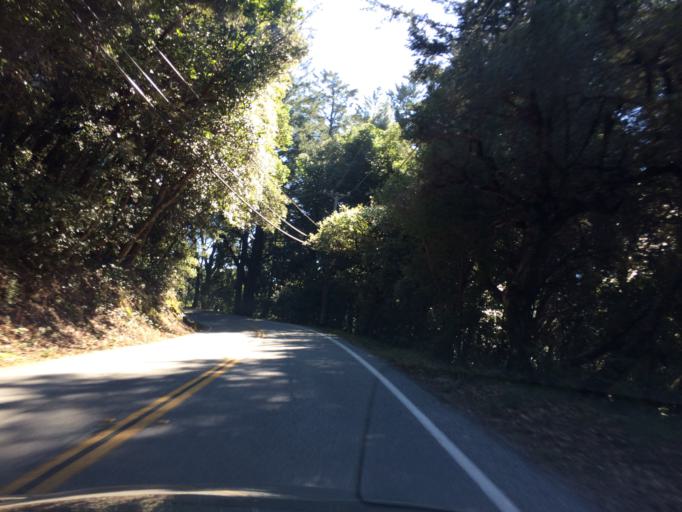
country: US
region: California
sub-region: Santa Cruz County
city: Boulder Creek
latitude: 37.0977
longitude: -122.1425
